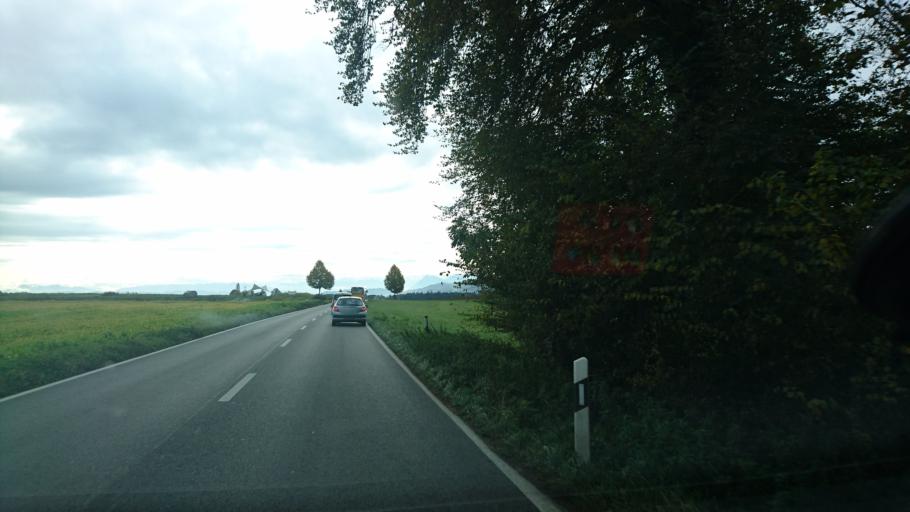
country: CH
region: Bern
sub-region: Bern-Mittelland District
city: Kirchlindach
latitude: 46.9840
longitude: 7.4144
